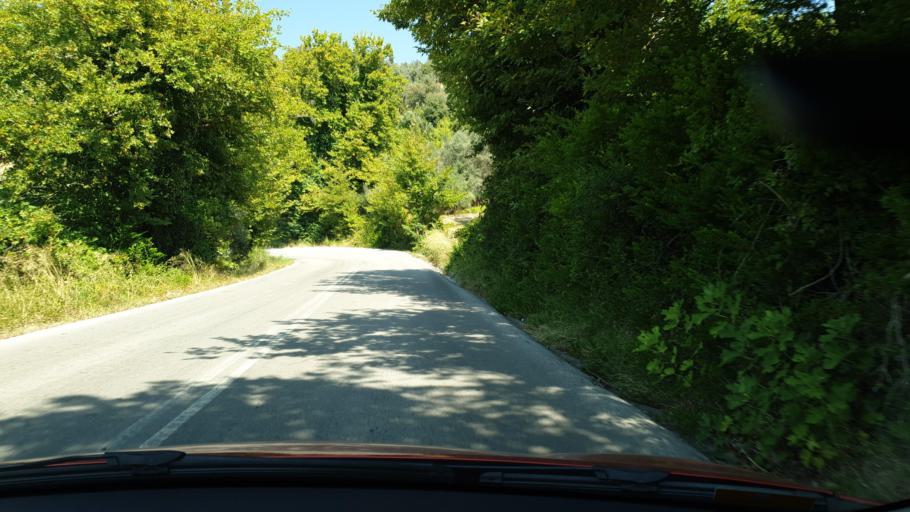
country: GR
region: Central Greece
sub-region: Nomos Evvoias
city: Kymi
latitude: 38.6082
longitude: 24.0748
